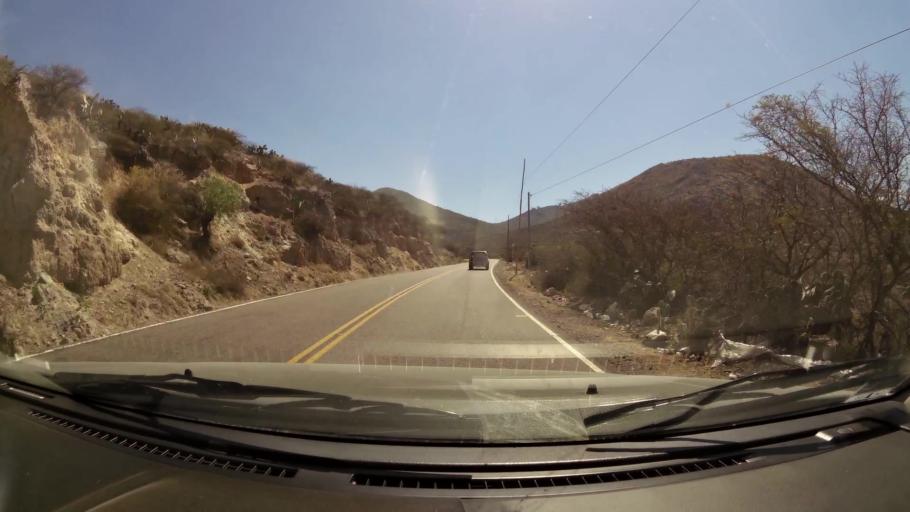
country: PE
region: Ayacucho
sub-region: Provincia de Huamanga
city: Pacaycasa
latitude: -13.0609
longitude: -74.2288
